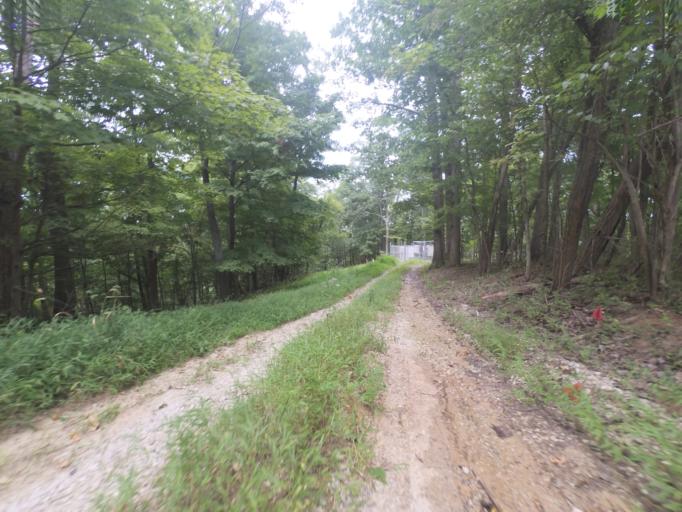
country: US
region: West Virginia
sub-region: Cabell County
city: Huntington
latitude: 38.3941
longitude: -82.4600
